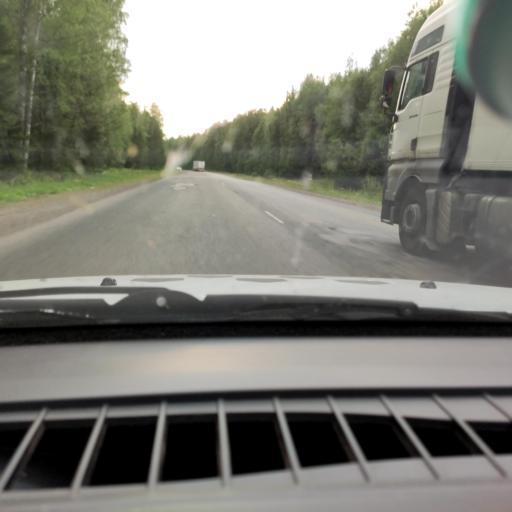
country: RU
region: Udmurtiya
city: Igra
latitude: 57.6007
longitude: 53.3103
